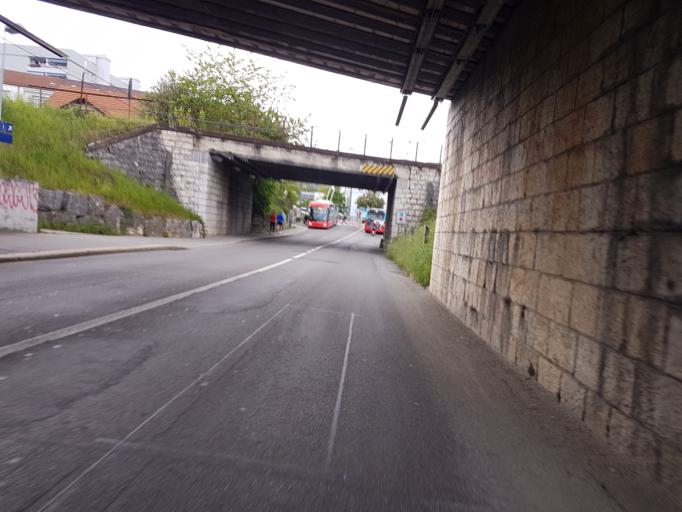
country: CH
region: Bern
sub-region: Biel/Bienne District
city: Brugg
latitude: 47.1456
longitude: 7.2736
